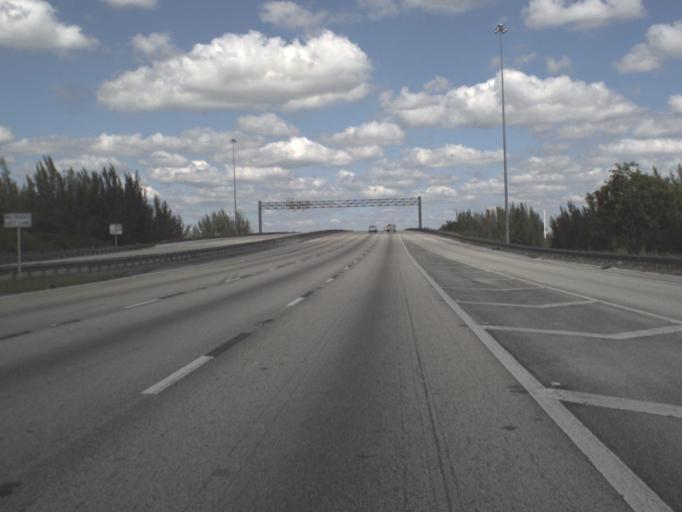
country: US
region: Florida
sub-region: Miami-Dade County
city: Doral
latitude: 25.8727
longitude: -80.3879
